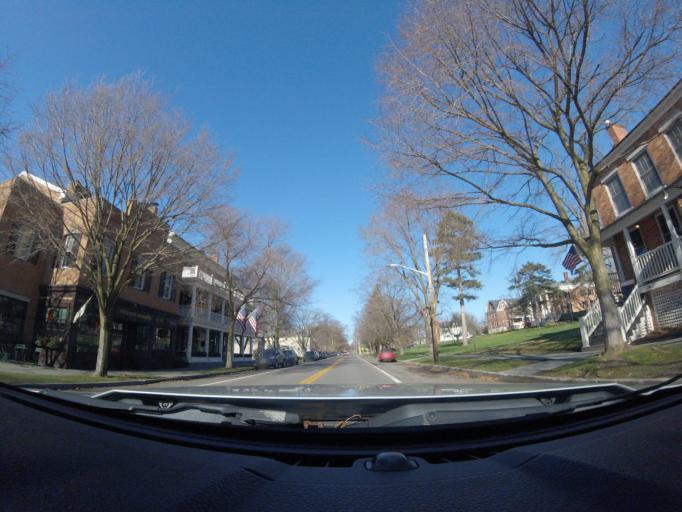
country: US
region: New York
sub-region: Cayuga County
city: Union Springs
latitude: 42.7542
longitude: -76.7025
